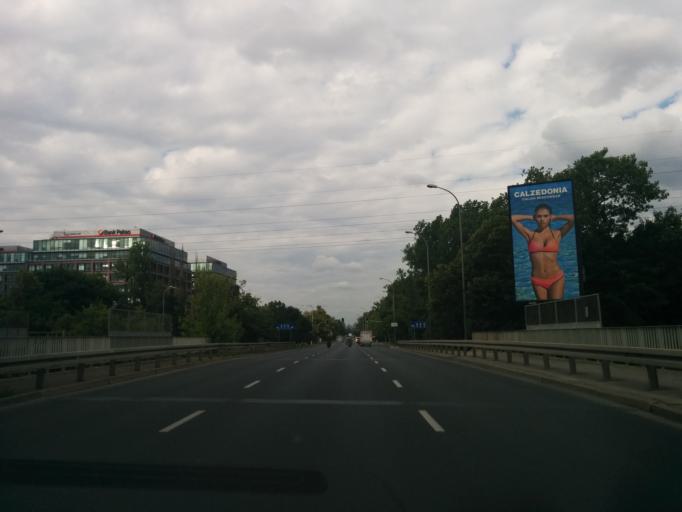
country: PL
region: Masovian Voivodeship
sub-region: Warszawa
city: Ochota
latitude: 52.1926
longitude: 20.9821
